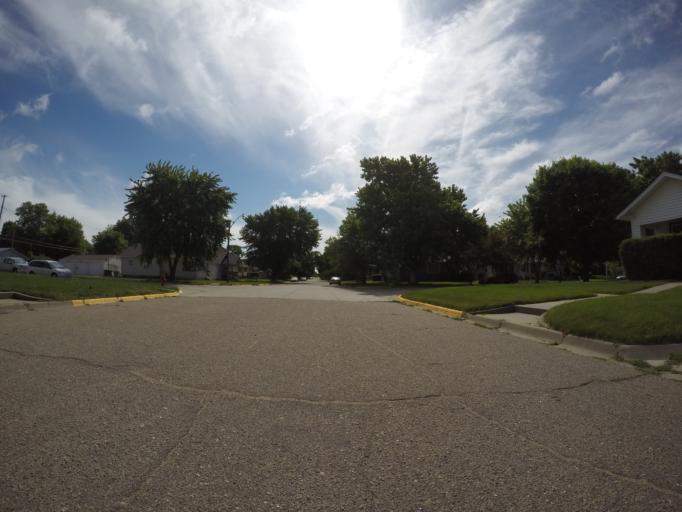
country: US
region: Nebraska
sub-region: Buffalo County
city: Kearney
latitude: 40.7036
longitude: -99.0914
